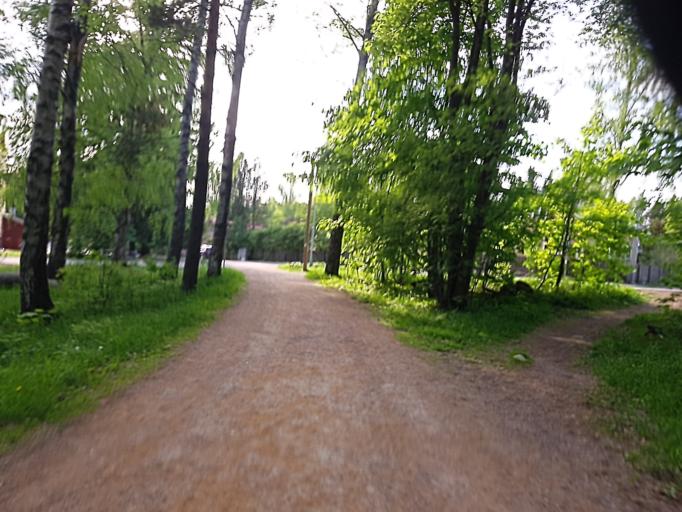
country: FI
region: Uusimaa
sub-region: Helsinki
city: Helsinki
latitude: 60.2439
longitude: 24.9374
